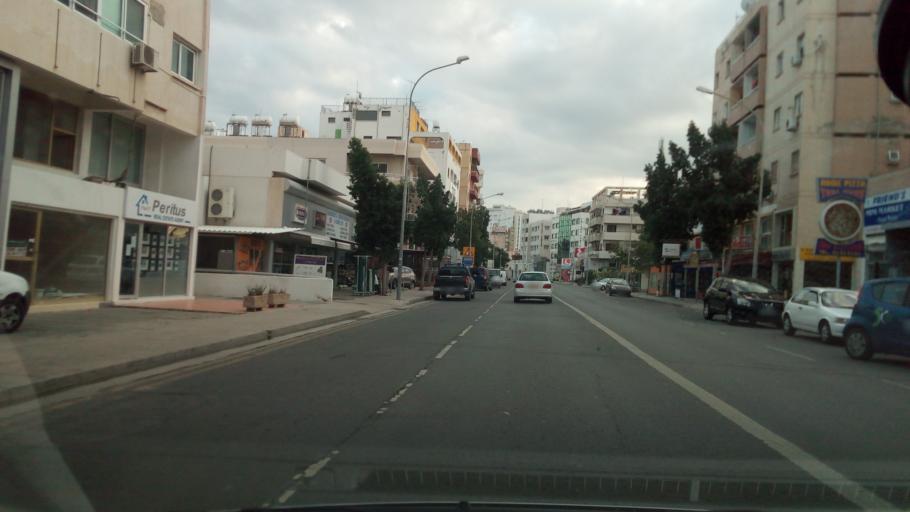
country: CY
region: Larnaka
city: Larnaca
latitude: 34.9236
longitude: 33.6368
